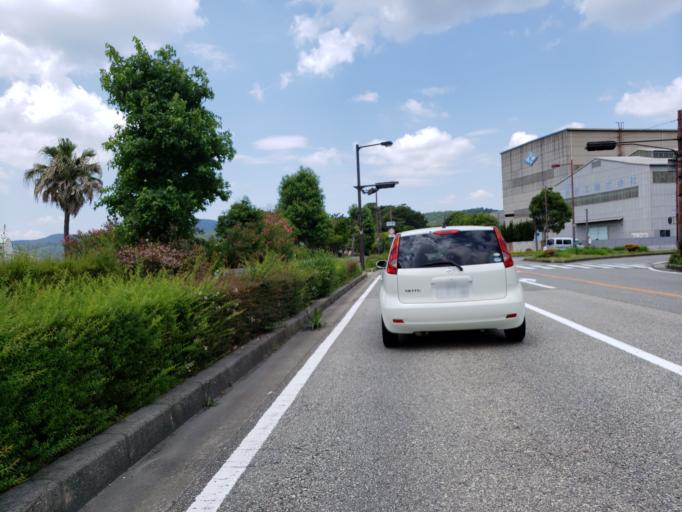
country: JP
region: Hyogo
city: Aioi
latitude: 34.8020
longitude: 134.4669
